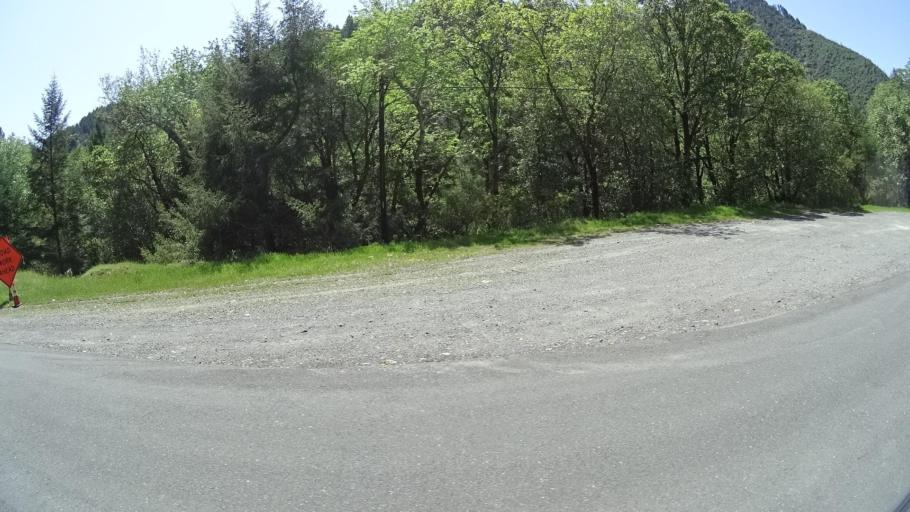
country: US
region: California
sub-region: Humboldt County
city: Redway
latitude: 40.2281
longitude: -123.6091
